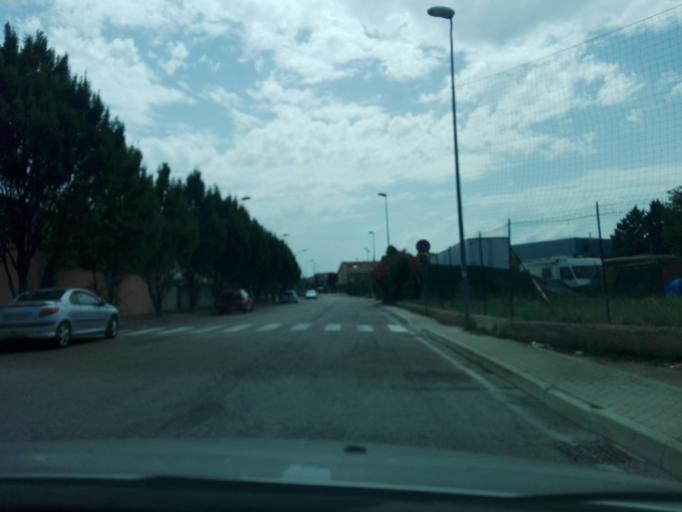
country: IT
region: Abruzzo
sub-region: Provincia di Pescara
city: Montesilvano Marina
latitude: 42.5002
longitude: 14.1309
